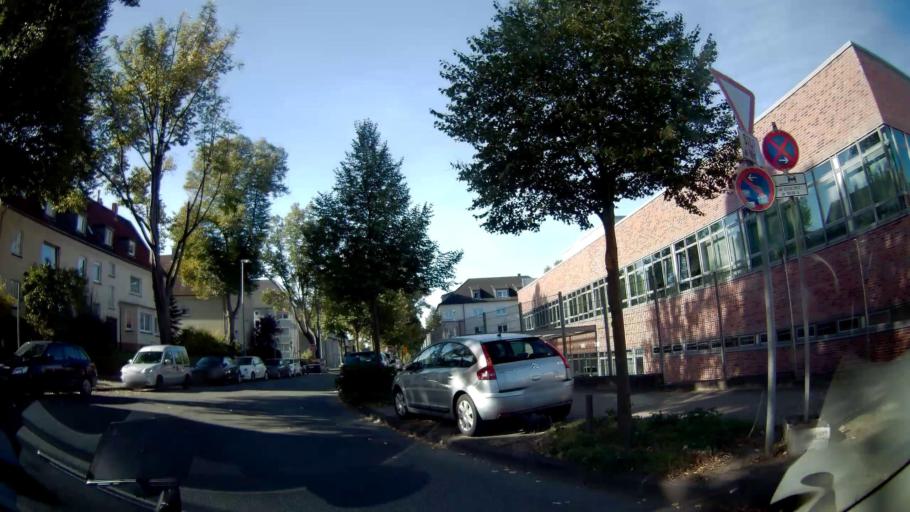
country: DE
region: North Rhine-Westphalia
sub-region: Regierungsbezirk Arnsberg
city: Bochum
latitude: 51.4669
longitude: 7.2118
